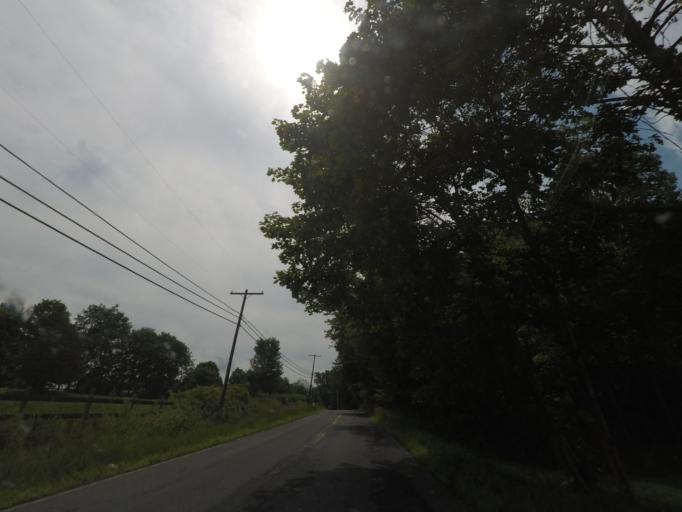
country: US
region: New York
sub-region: Rensselaer County
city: Wynantskill
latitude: 42.7509
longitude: -73.6058
